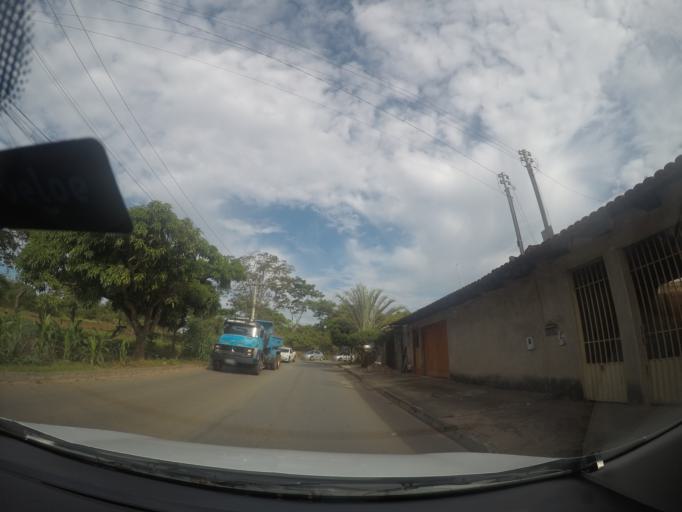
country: BR
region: Goias
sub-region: Goiania
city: Goiania
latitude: -16.6973
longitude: -49.1964
